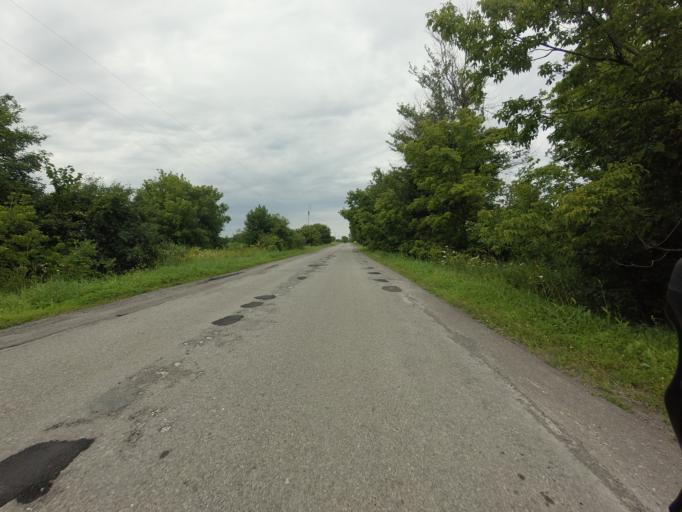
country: CA
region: Ontario
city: Bells Corners
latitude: 45.1077
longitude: -75.5955
